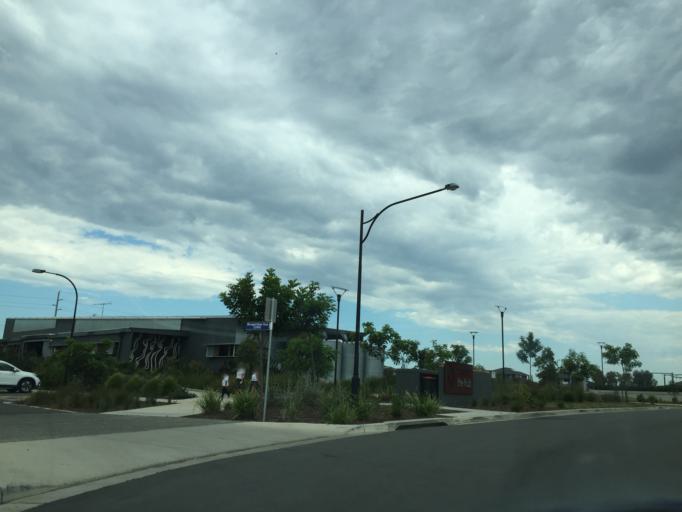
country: AU
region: New South Wales
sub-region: Blacktown
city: Doonside
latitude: -33.7779
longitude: 150.8718
